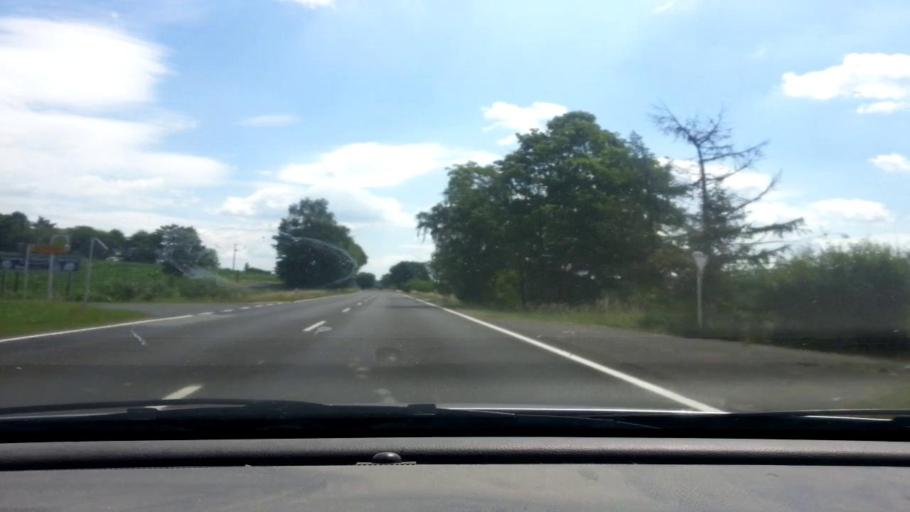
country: DE
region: Bavaria
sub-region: Upper Palatinate
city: Erbendorf
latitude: 49.8535
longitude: 11.9739
